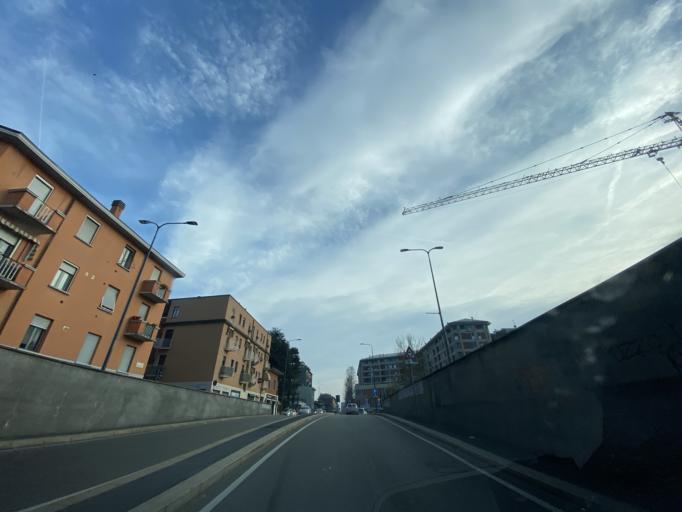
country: IT
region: Lombardy
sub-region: Citta metropolitana di Milano
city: Cormano
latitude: 45.5215
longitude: 9.1686
